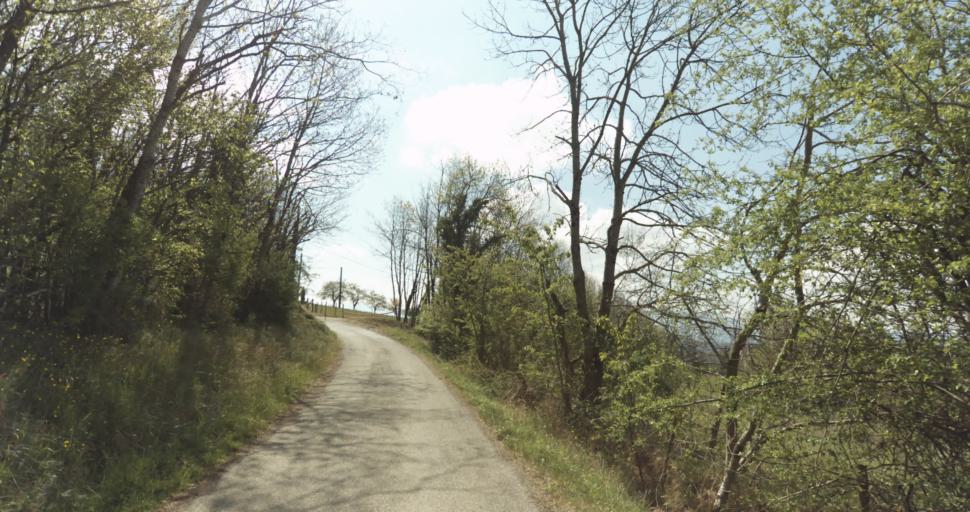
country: FR
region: Rhone-Alpes
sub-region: Departement de l'Isere
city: Saint-Marcellin
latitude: 45.1569
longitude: 5.3026
